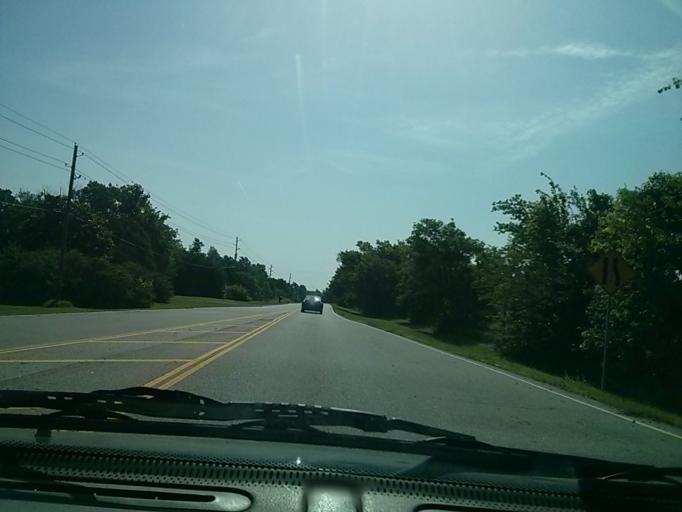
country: US
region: Oklahoma
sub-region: Tulsa County
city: Broken Arrow
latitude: 36.1334
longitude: -95.8125
